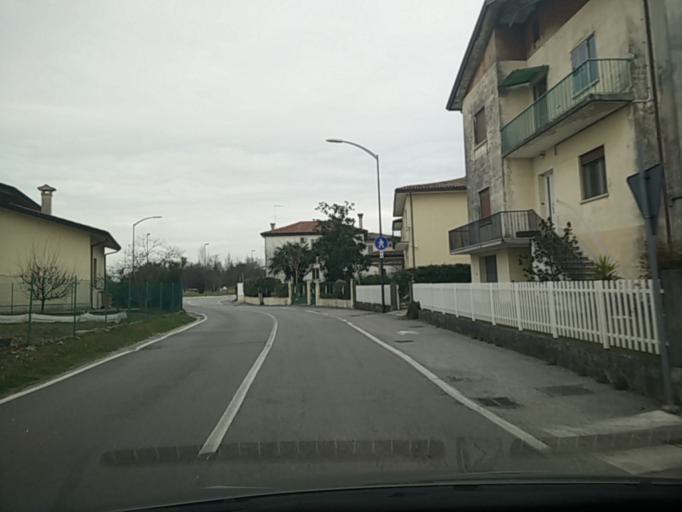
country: IT
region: Veneto
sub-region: Provincia di Treviso
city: Treviso
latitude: 45.6541
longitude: 12.2241
